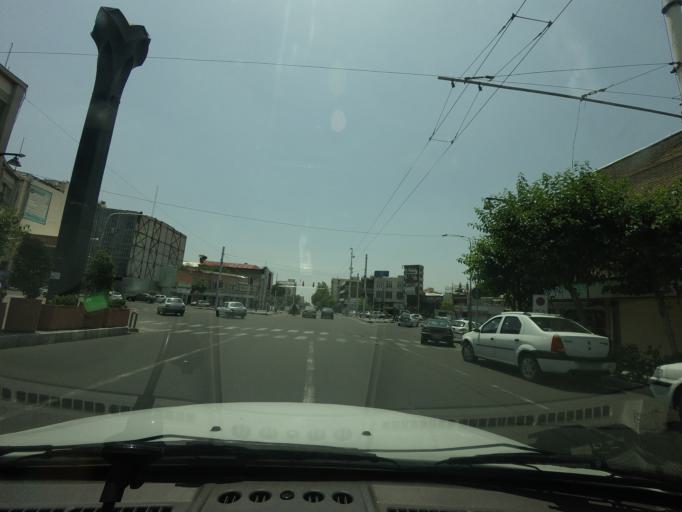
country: IR
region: Tehran
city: Tehran
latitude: 35.6901
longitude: 51.4473
